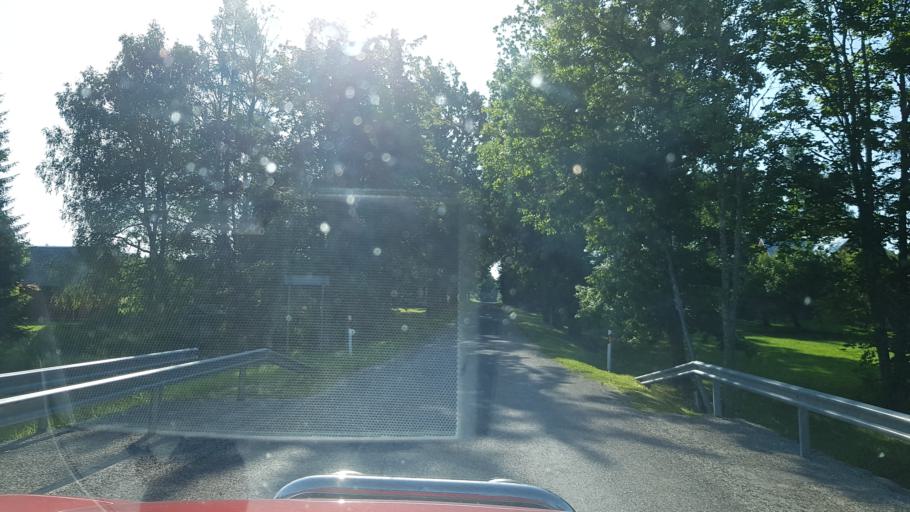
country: LV
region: Apes Novads
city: Ape
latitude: 57.6321
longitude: 26.7692
